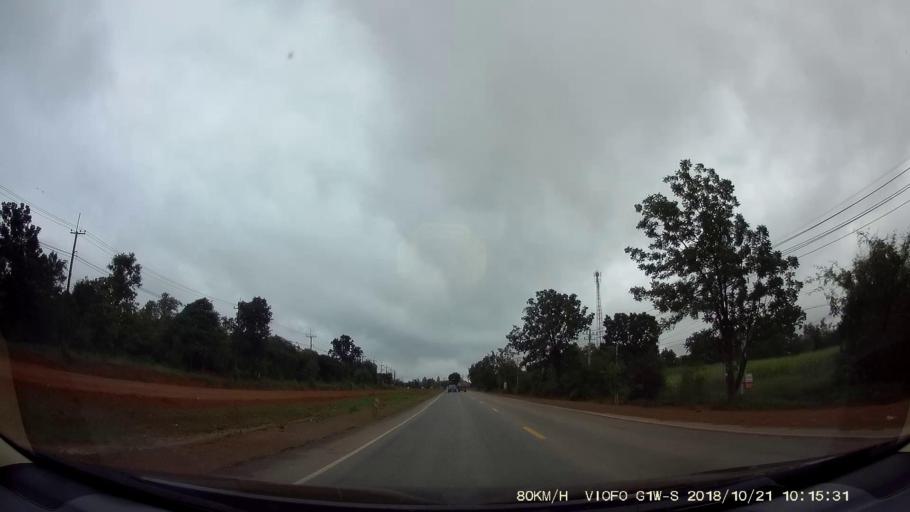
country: TH
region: Chaiyaphum
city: Phu Khiao
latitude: 16.3405
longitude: 102.1661
